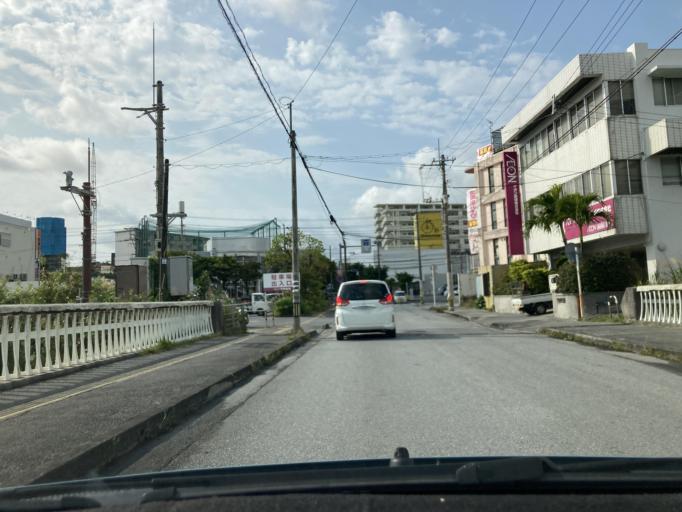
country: JP
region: Okinawa
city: Tomigusuku
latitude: 26.1966
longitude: 127.7195
